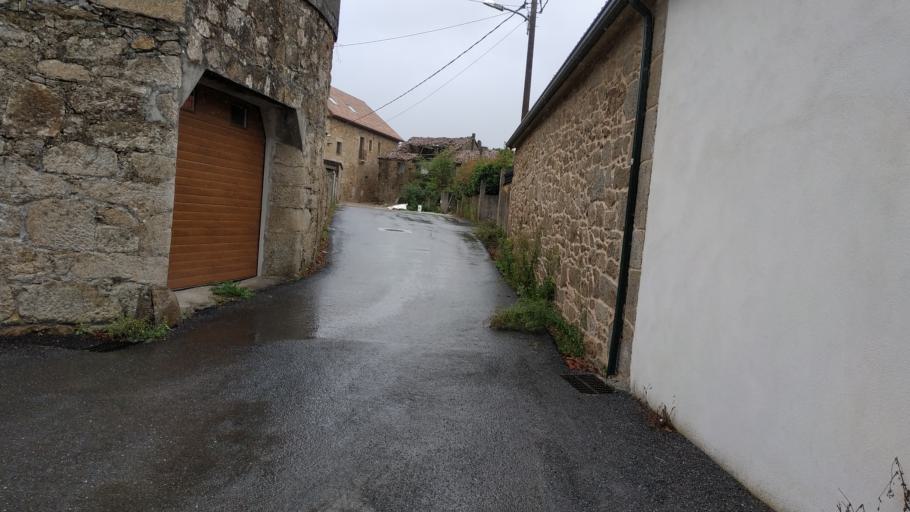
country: ES
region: Galicia
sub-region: Provincia da Coruna
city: Negreira
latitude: 42.9092
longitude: -8.7415
